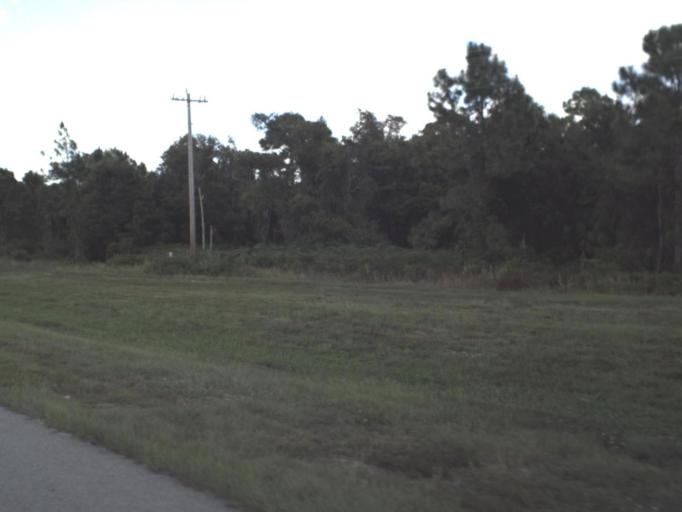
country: US
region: Florida
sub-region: Lee County
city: Lehigh Acres
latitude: 26.5473
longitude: -81.6398
